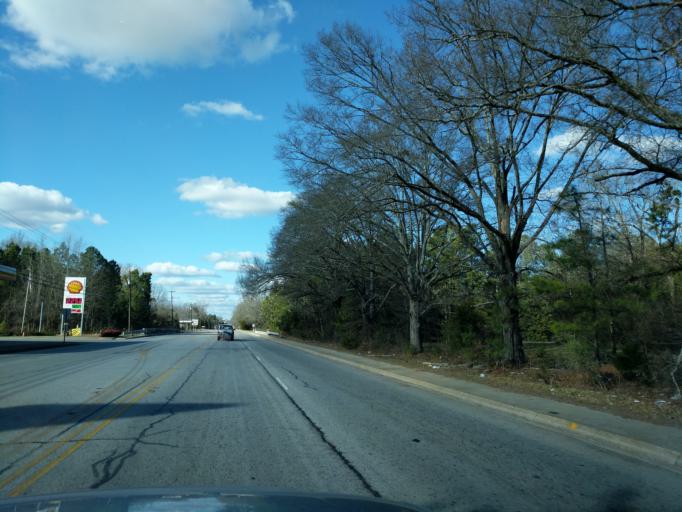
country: US
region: South Carolina
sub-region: Greenwood County
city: Greenwood
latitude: 34.1367
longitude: -82.1297
